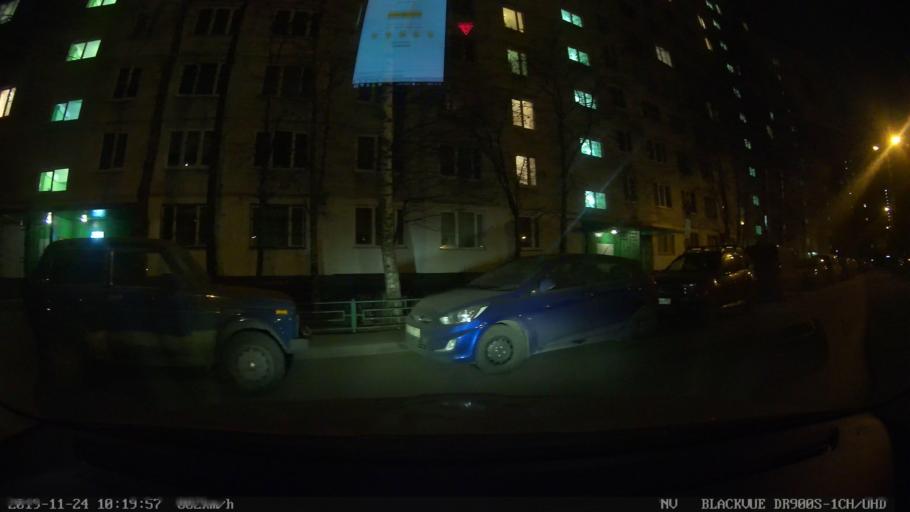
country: RU
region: Moscow
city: Bibirevo
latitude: 55.8908
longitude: 37.5949
